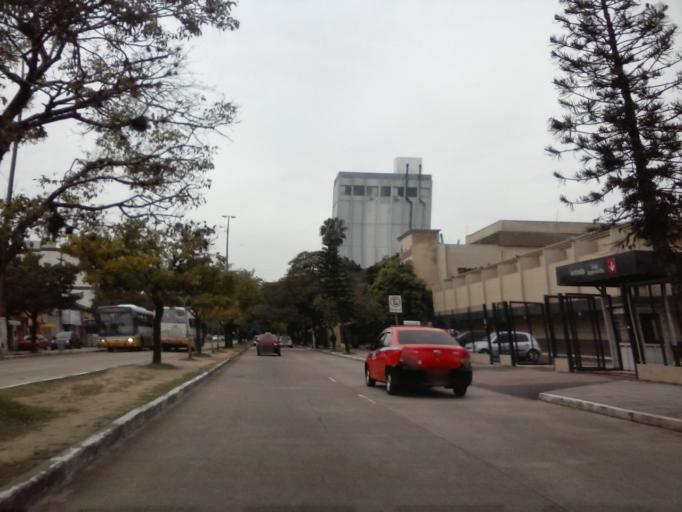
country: BR
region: Rio Grande do Sul
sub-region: Porto Alegre
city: Porto Alegre
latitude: -30.0435
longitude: -51.2242
